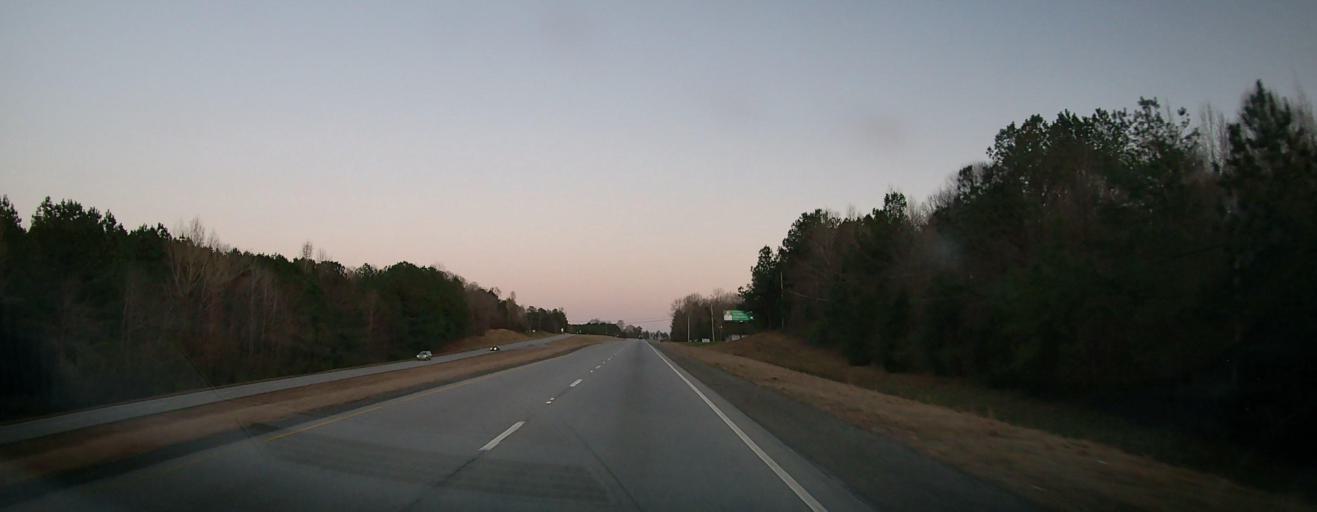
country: US
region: Alabama
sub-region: Tallapoosa County
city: Dadeville
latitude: 32.8722
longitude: -85.8078
